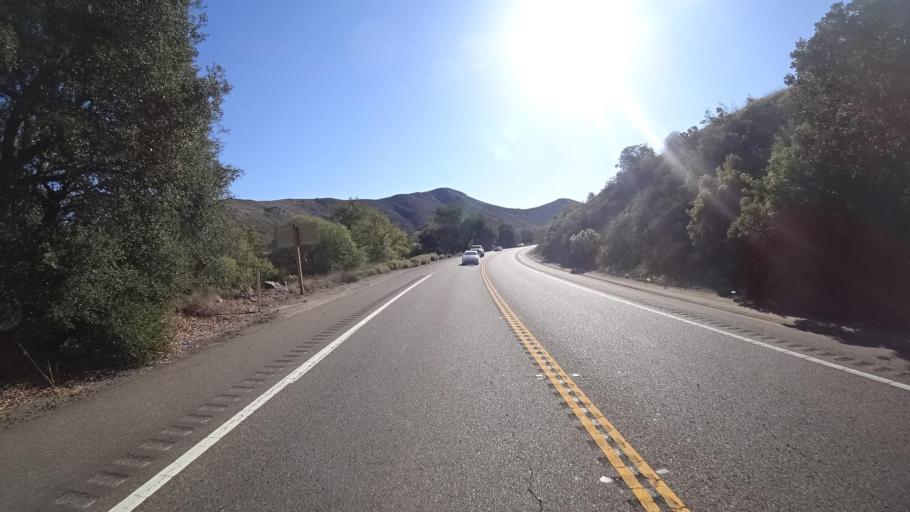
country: US
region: California
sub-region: San Diego County
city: Jamul
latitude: 32.6642
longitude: -116.8155
